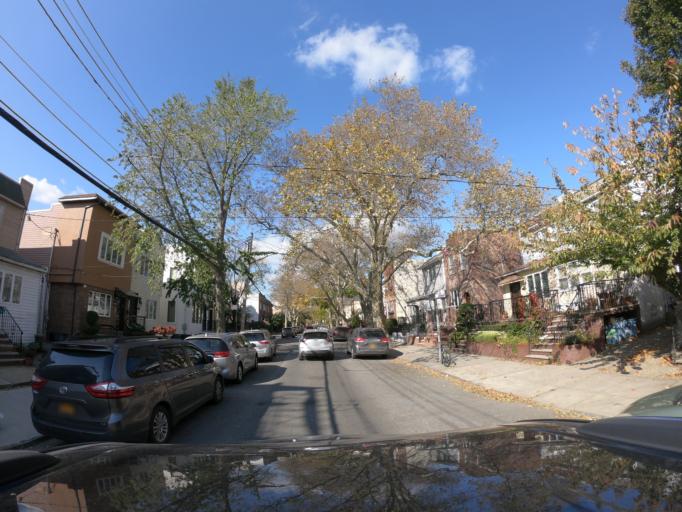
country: US
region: New York
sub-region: Kings County
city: Bensonhurst
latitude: 40.6237
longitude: -73.9794
